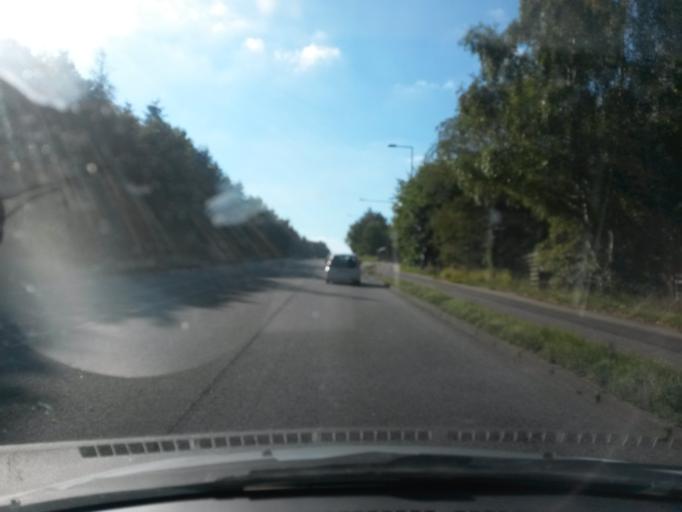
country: DK
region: Central Jutland
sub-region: Silkeborg Kommune
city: Silkeborg
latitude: 56.1501
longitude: 9.4827
